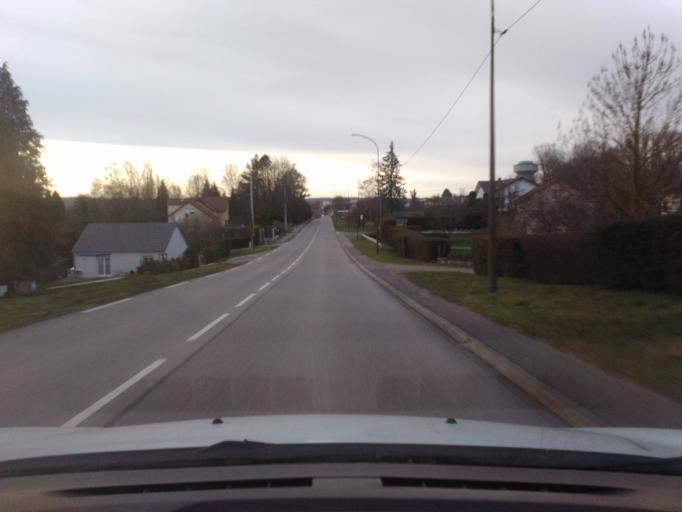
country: FR
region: Lorraine
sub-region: Departement des Vosges
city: Charmes
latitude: 48.3732
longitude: 6.3073
